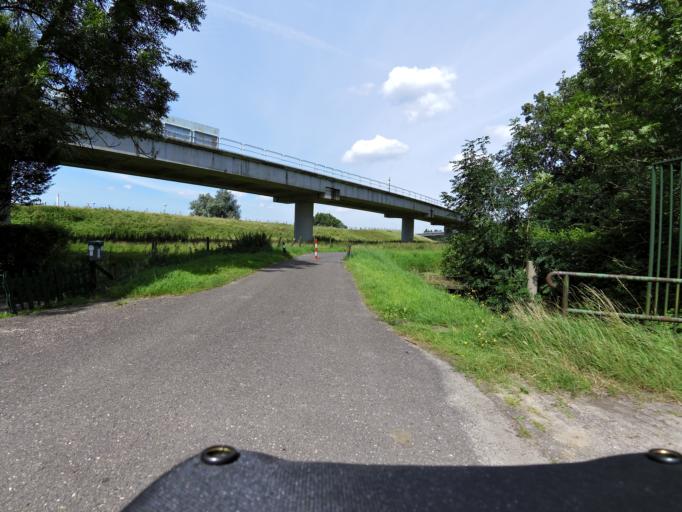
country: NL
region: South Holland
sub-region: Gemeente Albrandswaard
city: Rhoon
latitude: 51.8625
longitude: 4.3818
